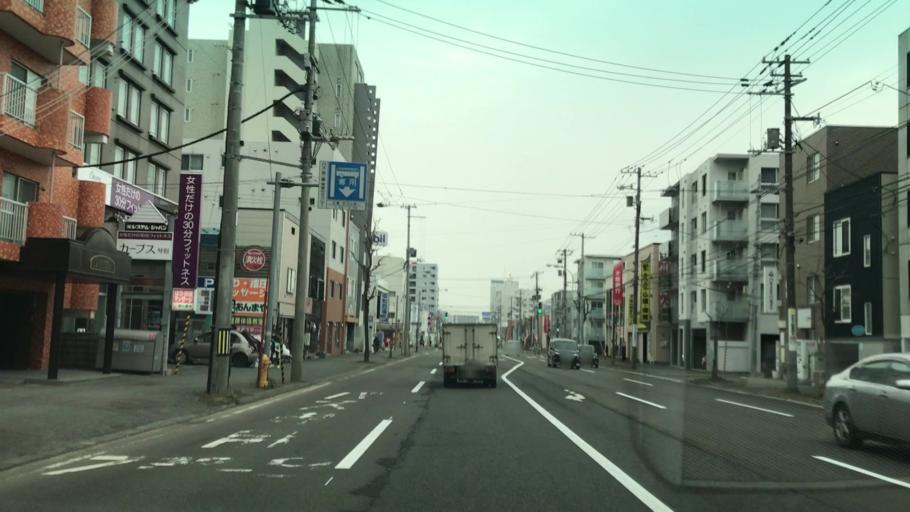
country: JP
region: Hokkaido
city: Sapporo
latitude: 43.0724
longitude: 141.3005
